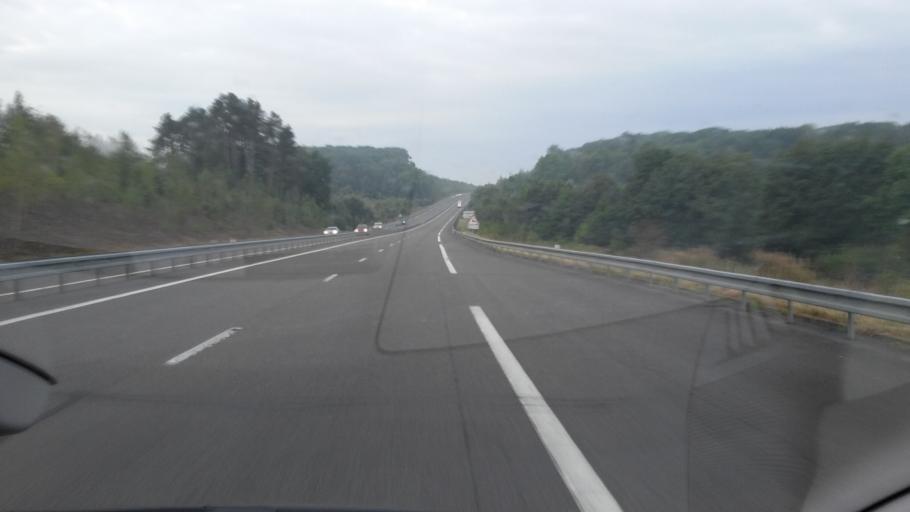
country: FR
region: Champagne-Ardenne
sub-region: Departement des Ardennes
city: Attigny
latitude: 49.6171
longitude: 4.5440
